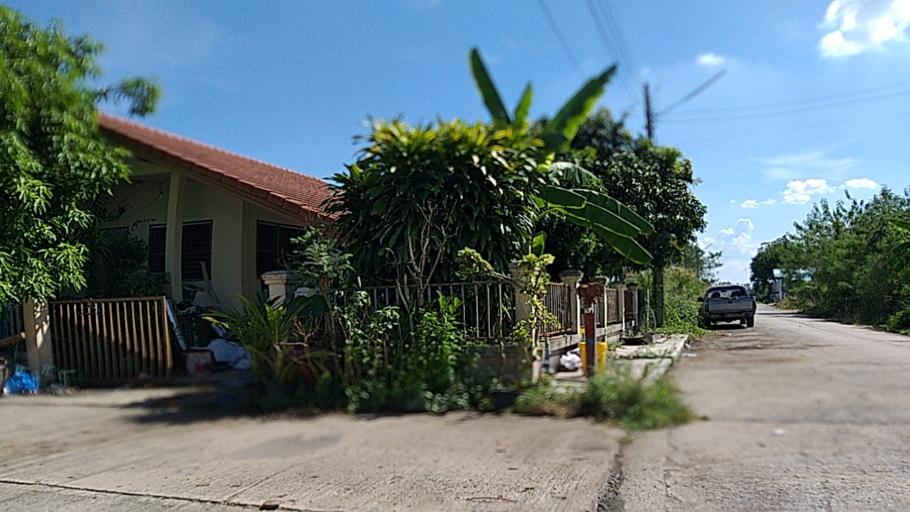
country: TH
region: Pathum Thani
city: Nong Suea
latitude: 14.0652
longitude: 100.8704
